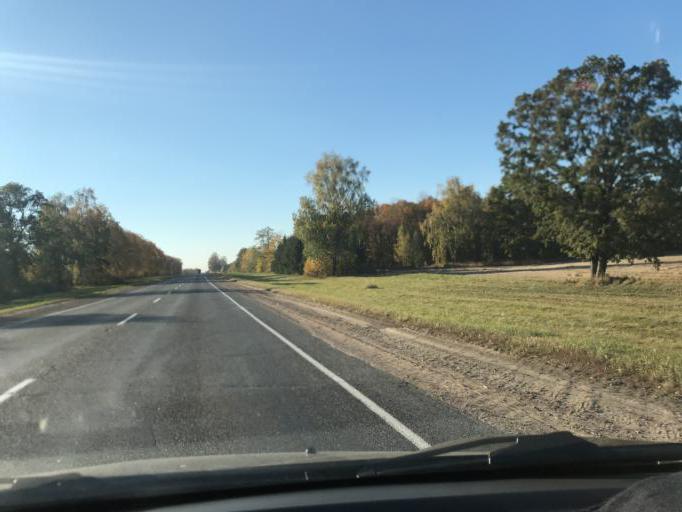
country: BY
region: Minsk
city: Urechcha
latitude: 53.0742
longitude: 27.7689
